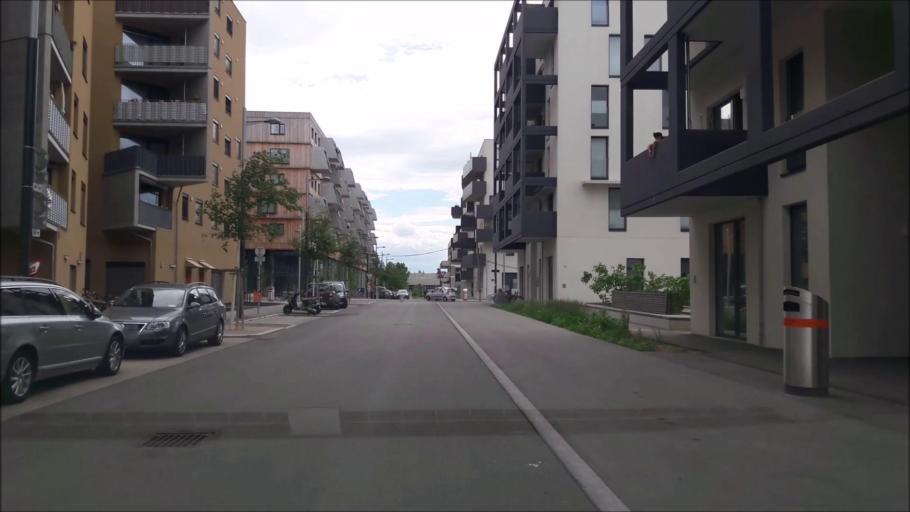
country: AT
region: Lower Austria
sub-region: Politischer Bezirk Ganserndorf
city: Gross-Enzersdorf
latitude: 48.2253
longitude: 16.4984
